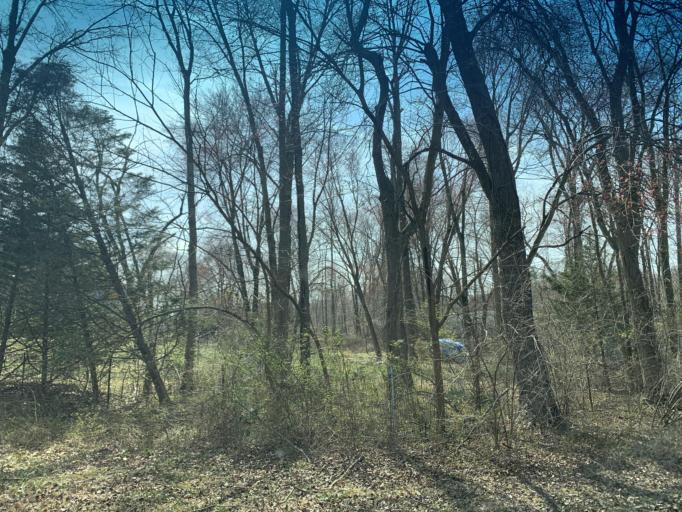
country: US
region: Maryland
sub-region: Cecil County
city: Charlestown
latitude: 39.5780
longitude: -75.9794
